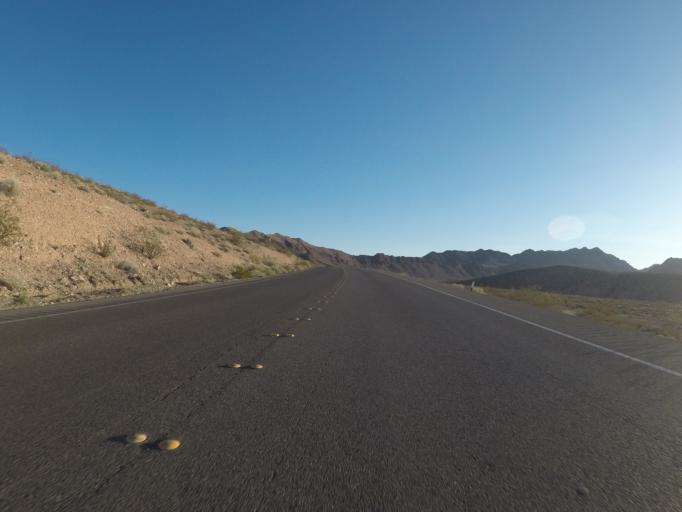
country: US
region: Nevada
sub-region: Clark County
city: Moapa Valley
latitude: 36.2673
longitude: -114.4830
